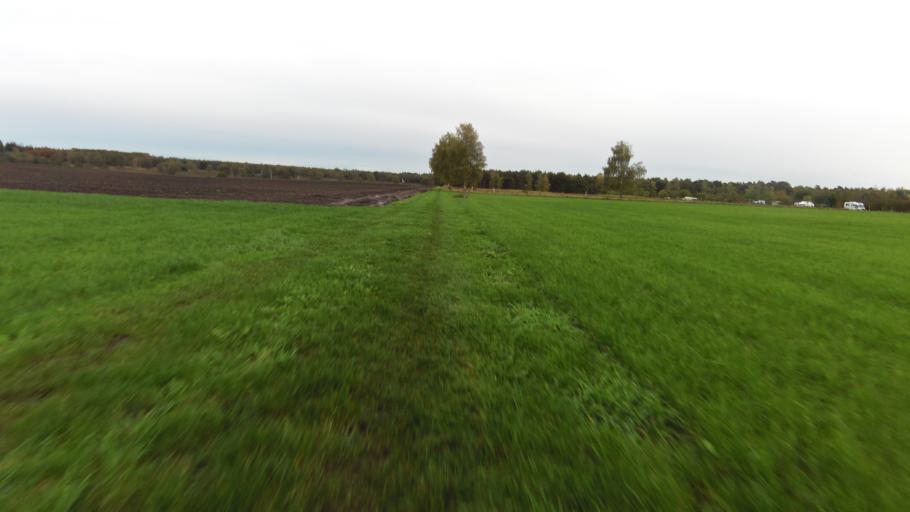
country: NL
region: Gelderland
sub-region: Gemeente Renkum
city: Wolfheze
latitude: 52.0104
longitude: 5.7998
